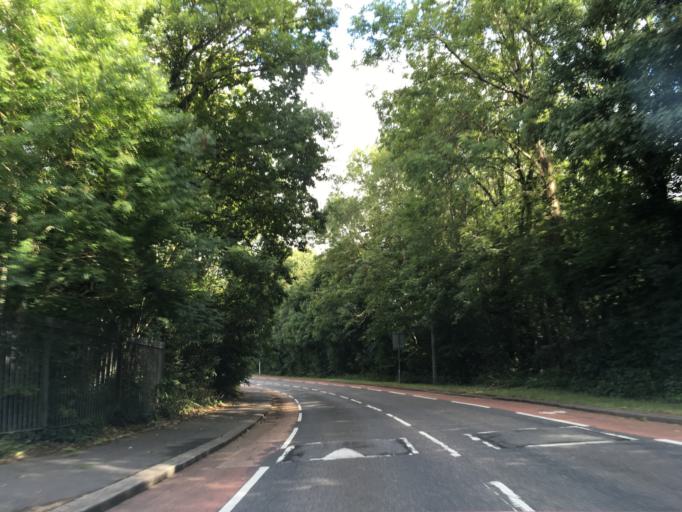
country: GB
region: Wales
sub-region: Cardiff
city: Cardiff
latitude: 51.5078
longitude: -3.1574
